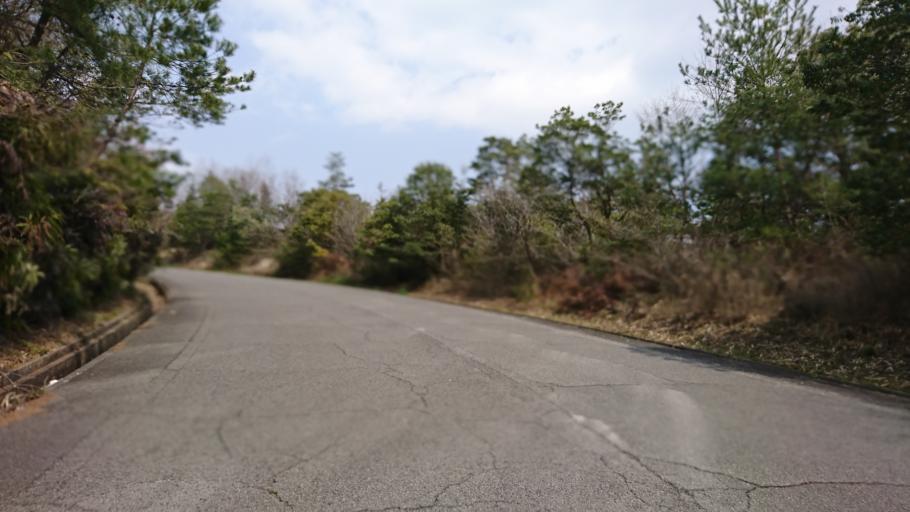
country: JP
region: Hyogo
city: Ono
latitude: 34.8184
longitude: 134.9037
